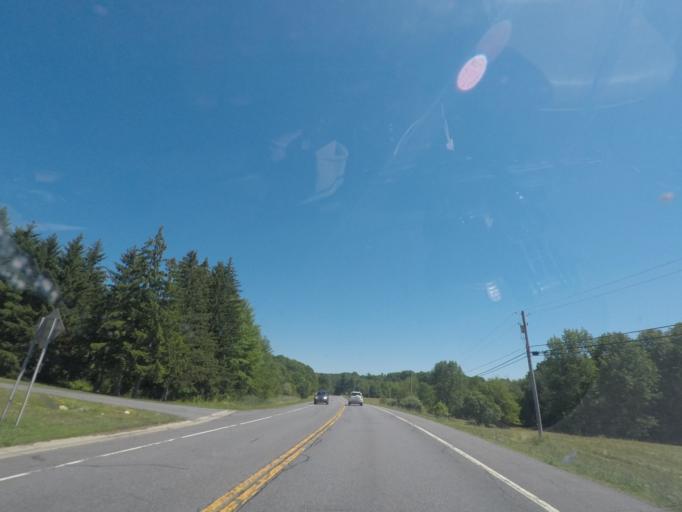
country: US
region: New York
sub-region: Rensselaer County
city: Averill Park
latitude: 42.6564
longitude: -73.5719
